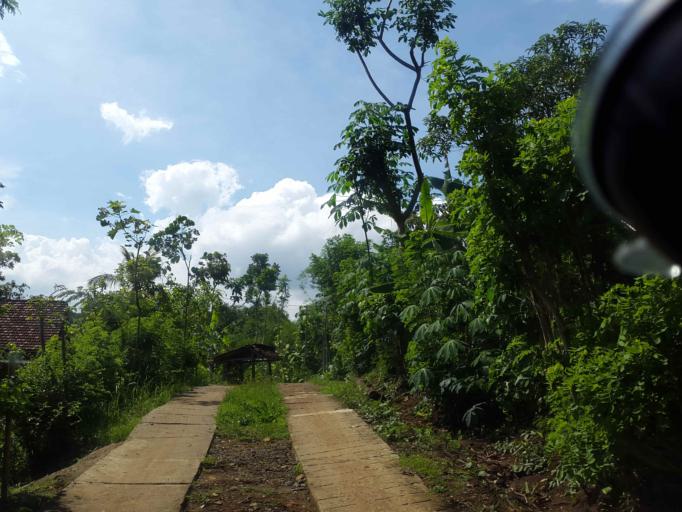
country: ID
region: East Java
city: Prambonkrajan
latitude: -8.0044
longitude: 111.6886
